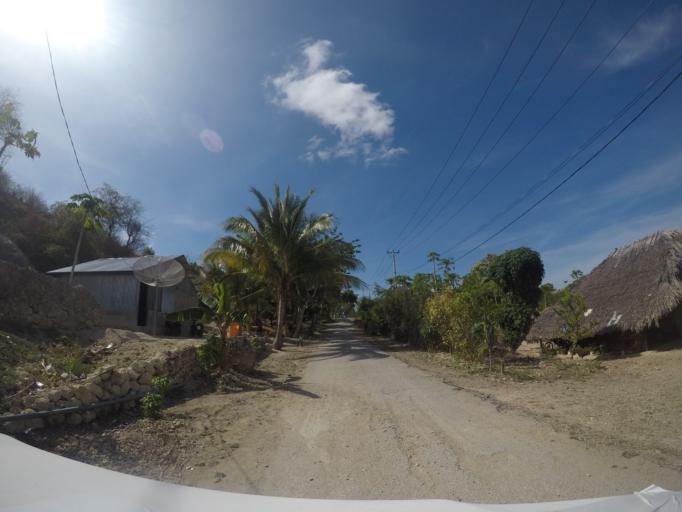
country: TL
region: Baucau
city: Baucau
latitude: -8.4660
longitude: 126.4706
